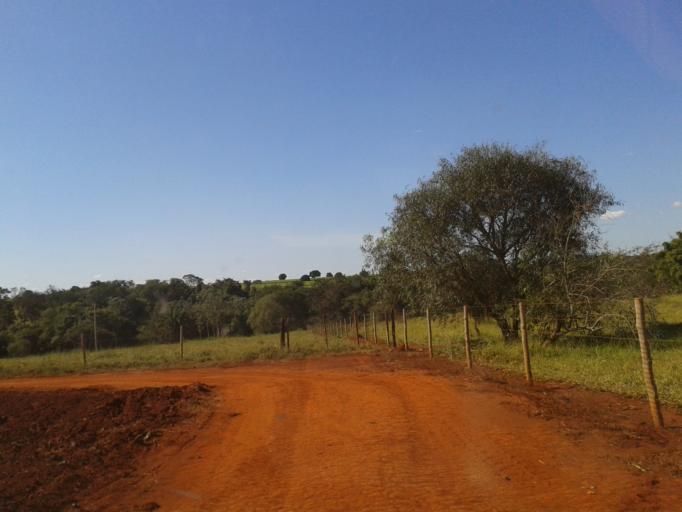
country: BR
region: Minas Gerais
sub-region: Centralina
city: Centralina
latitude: -18.5914
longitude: -49.2756
